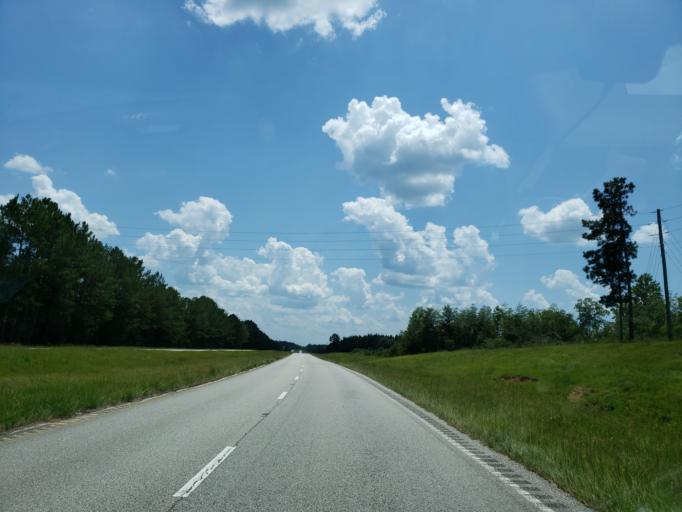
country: US
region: Mississippi
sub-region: Wayne County
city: Belmont
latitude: 31.3899
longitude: -88.4788
